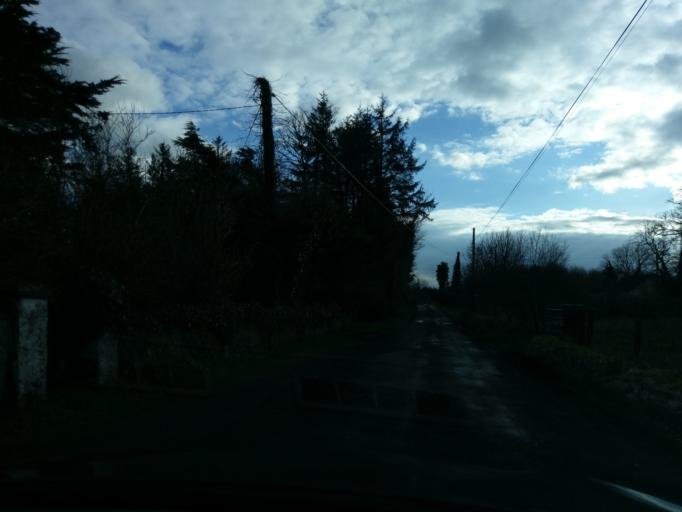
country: IE
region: Connaught
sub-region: County Galway
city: Athenry
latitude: 53.3783
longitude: -8.6268
